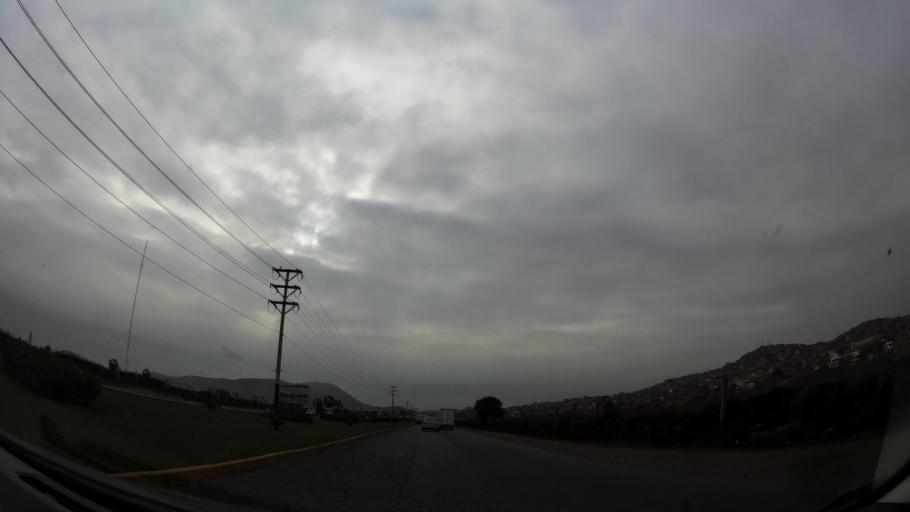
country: PE
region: Lima
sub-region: Lima
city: Surco
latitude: -12.2039
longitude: -76.9927
